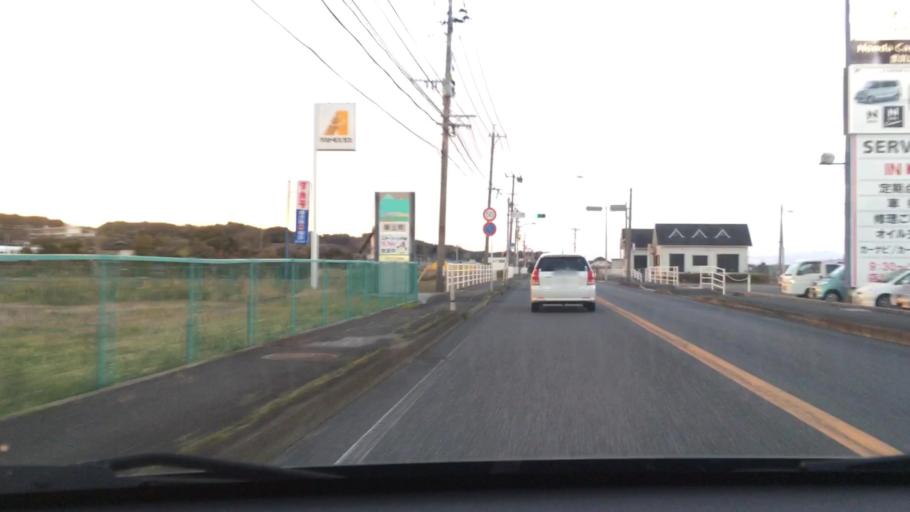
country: JP
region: Fukuoka
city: Shiida
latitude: 33.6300
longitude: 131.0847
